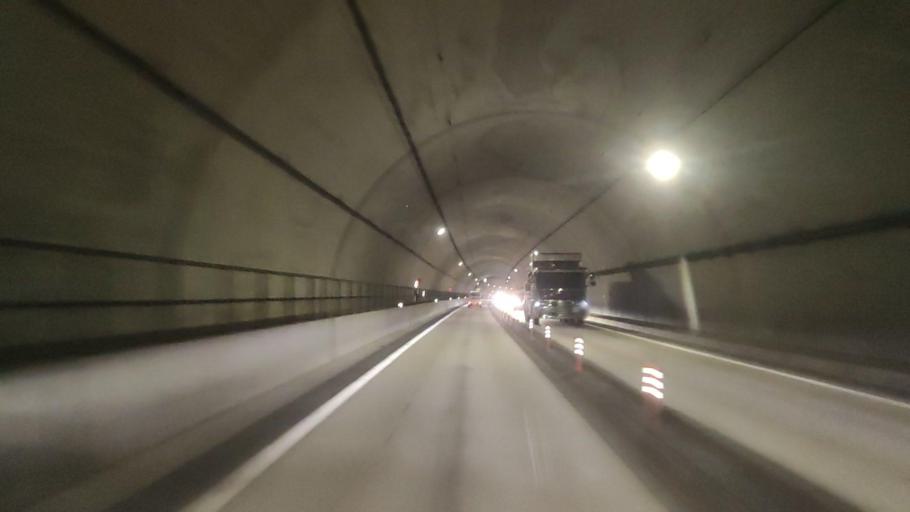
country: JP
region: Wakayama
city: Tanabe
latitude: 33.5880
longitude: 135.4437
